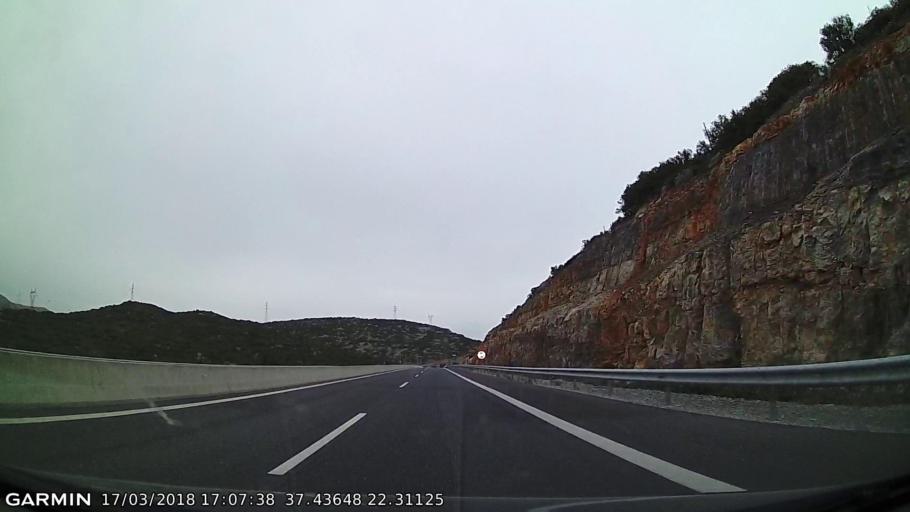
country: GR
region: Peloponnese
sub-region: Nomos Arkadias
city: Tripoli
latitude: 37.4372
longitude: 22.3112
